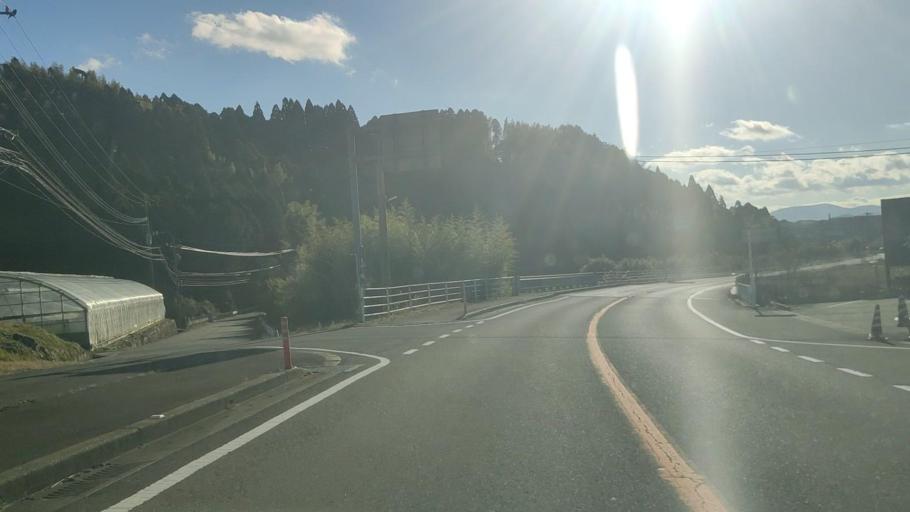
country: JP
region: Fukuoka
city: Maebaru-chuo
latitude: 33.4504
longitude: 130.2756
